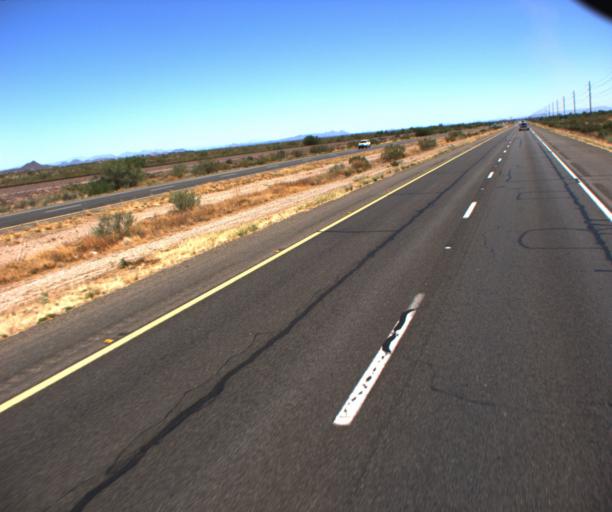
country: US
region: Arizona
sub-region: Maricopa County
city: Sun City West
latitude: 33.7299
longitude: -112.4674
